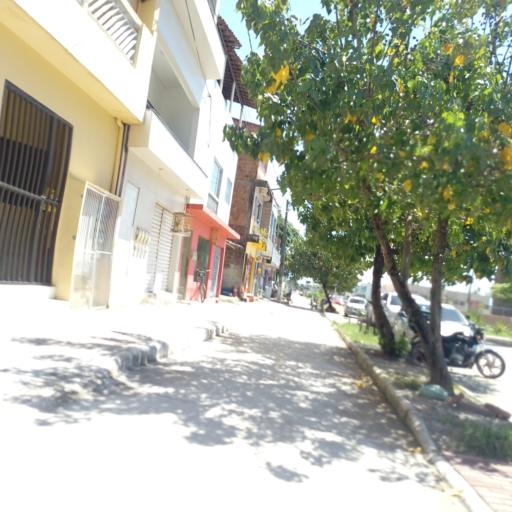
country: BR
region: Pernambuco
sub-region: Ipojuca
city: Ipojuca
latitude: -8.5097
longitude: -35.0090
